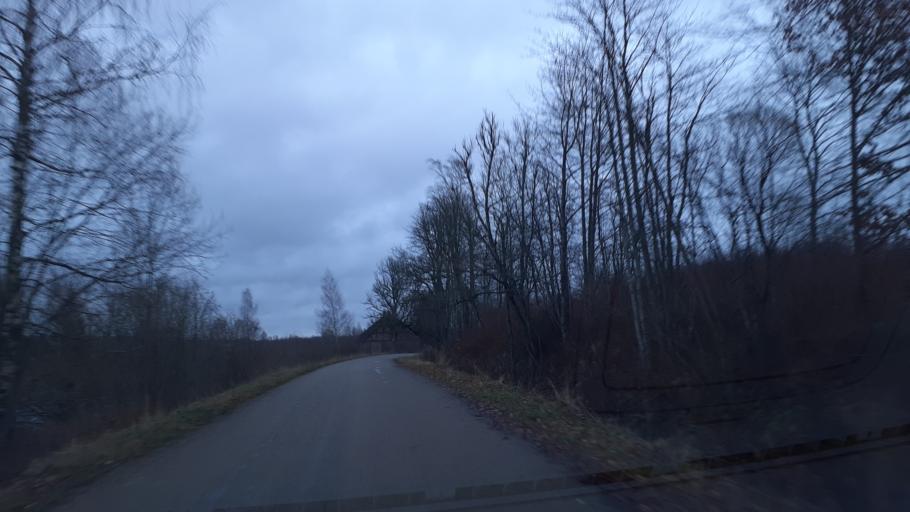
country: LV
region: Kuldigas Rajons
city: Kuldiga
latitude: 57.0426
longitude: 22.1321
